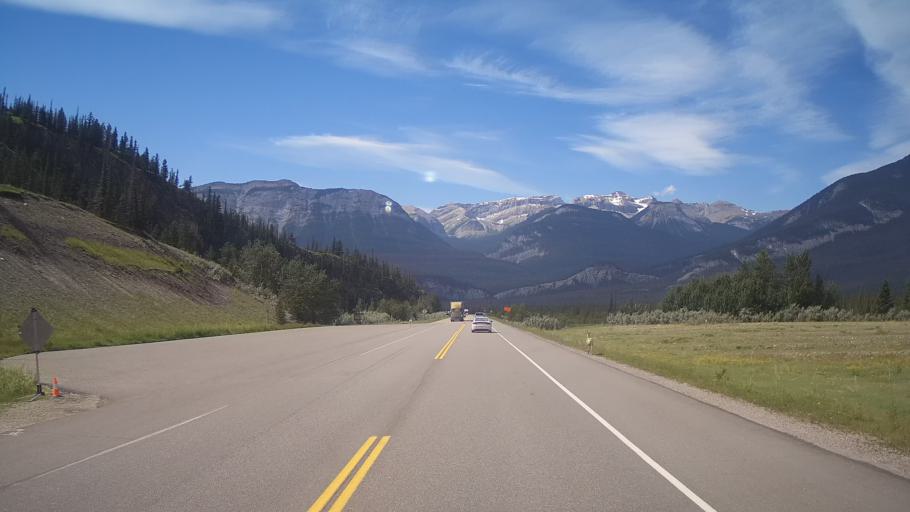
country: CA
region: Alberta
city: Jasper Park Lodge
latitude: 53.0451
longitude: -118.0824
